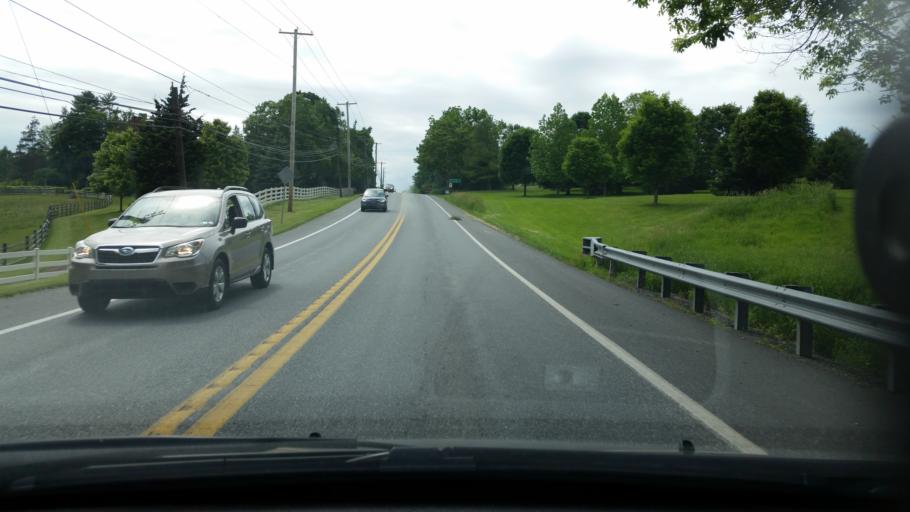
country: US
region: Pennsylvania
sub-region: Lancaster County
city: Elizabethtown
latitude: 40.1583
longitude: -76.6137
